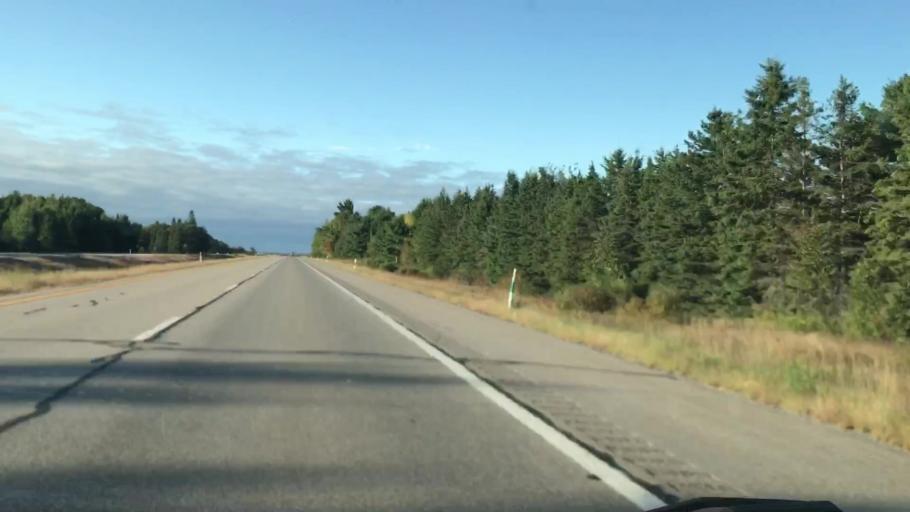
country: US
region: Michigan
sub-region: Chippewa County
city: Sault Ste. Marie
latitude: 46.4294
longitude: -84.3912
